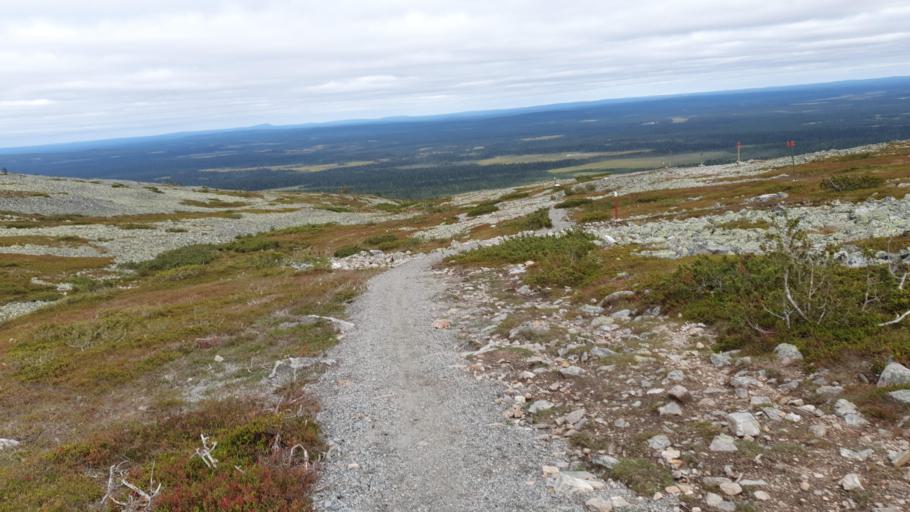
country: FI
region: Lapland
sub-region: Tunturi-Lappi
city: Kolari
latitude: 67.5684
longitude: 24.2419
